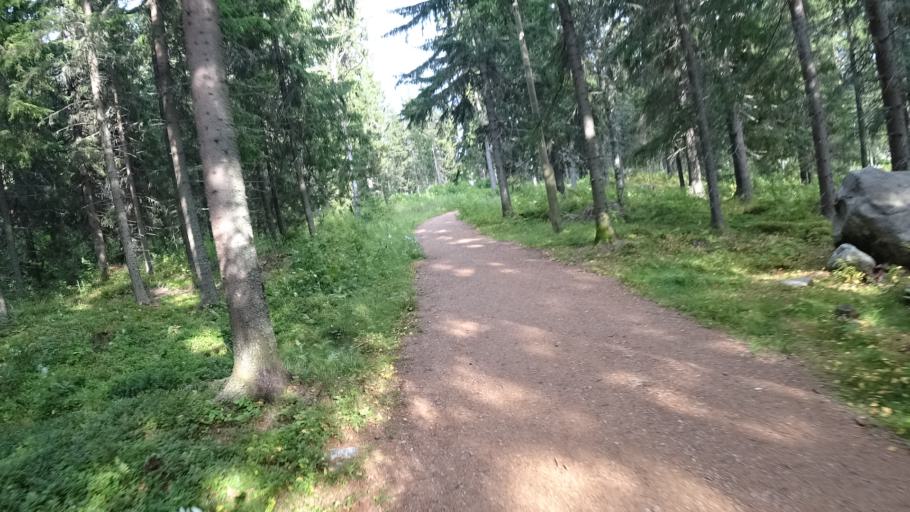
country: FI
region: North Karelia
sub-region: Joensuu
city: Ilomantsi
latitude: 62.6677
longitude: 30.9087
